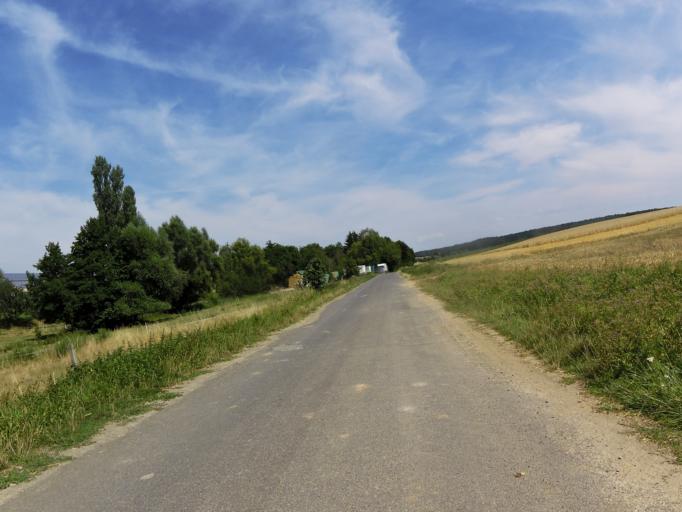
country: DE
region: Bavaria
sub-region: Regierungsbezirk Unterfranken
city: Estenfeld
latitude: 49.8113
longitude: 9.9992
